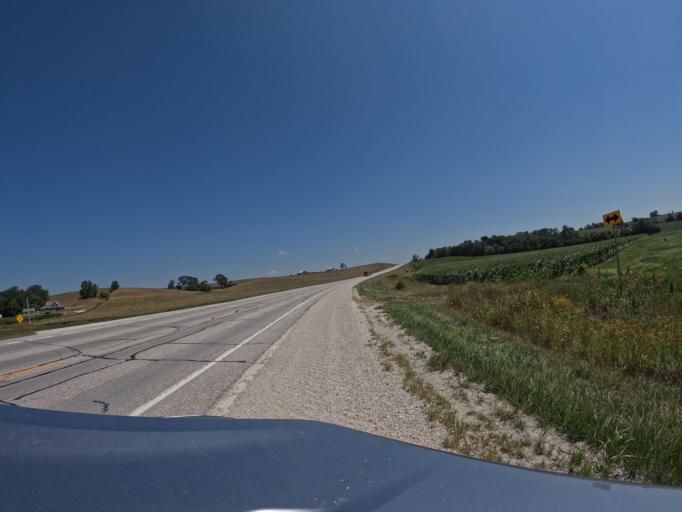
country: US
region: Iowa
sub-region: Keokuk County
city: Sigourney
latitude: 41.2421
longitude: -92.2133
